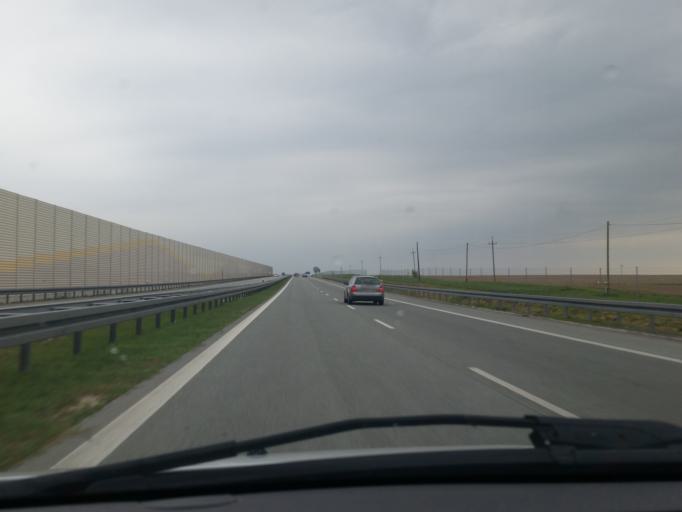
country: PL
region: Lodz Voivodeship
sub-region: Powiat skierniewicki
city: Kowiesy
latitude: 51.8544
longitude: 20.3731
